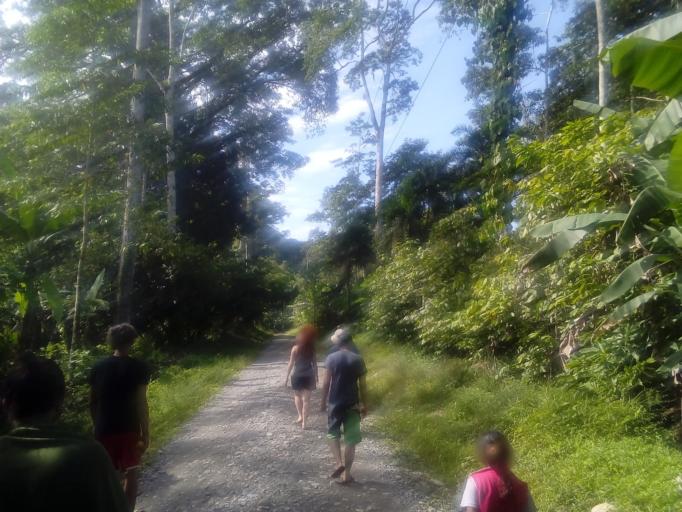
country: PA
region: Bocas del Toro
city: Barranco
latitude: 9.5108
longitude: -82.9804
